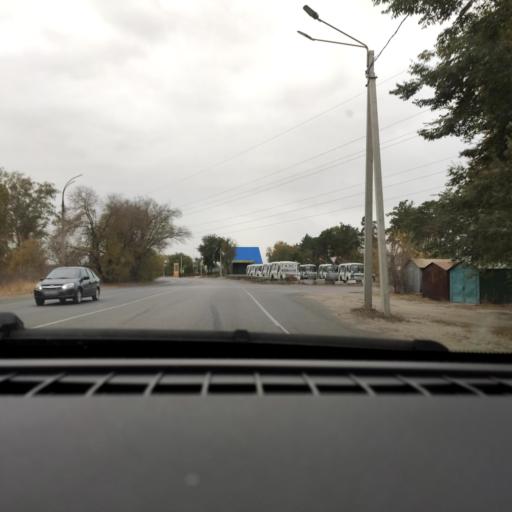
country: RU
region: Voronezj
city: Maslovka
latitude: 51.6322
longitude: 39.2878
